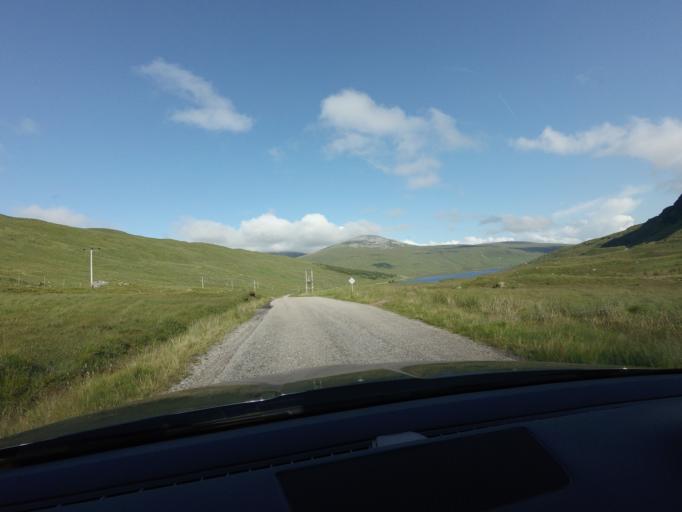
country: GB
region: Scotland
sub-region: Highland
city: Ullapool
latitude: 58.2575
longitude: -4.7847
